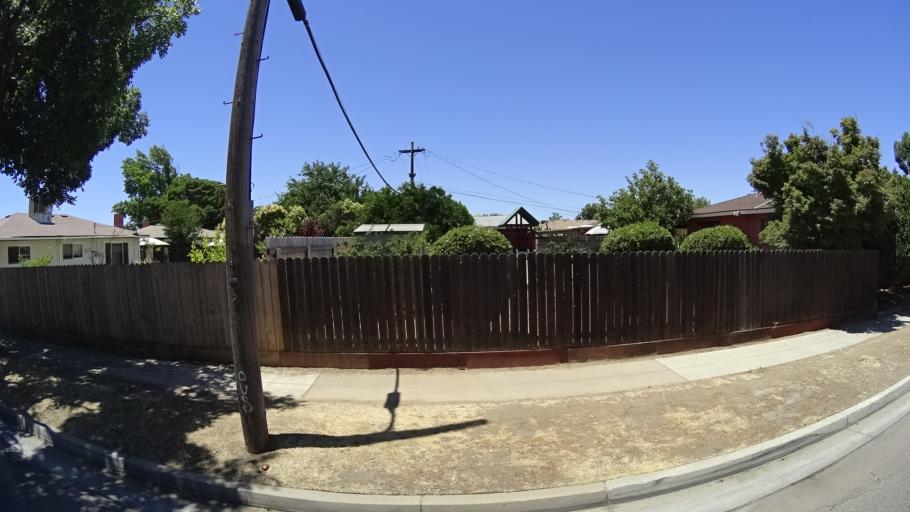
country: US
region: California
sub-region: Fresno County
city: Tarpey Village
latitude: 36.7993
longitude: -119.7498
